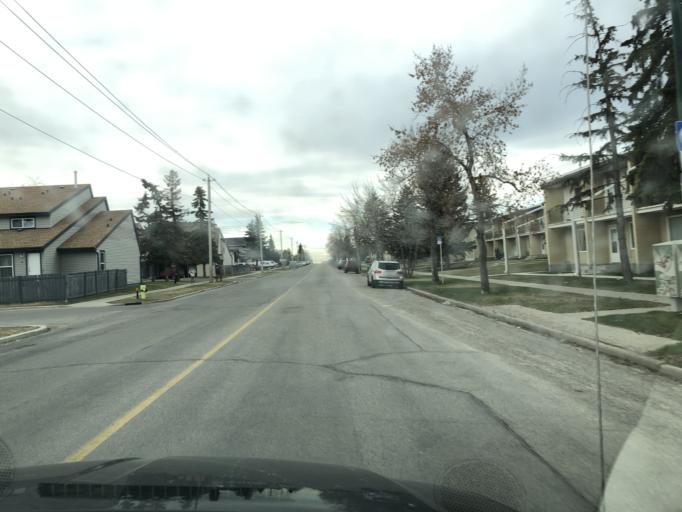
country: CA
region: Alberta
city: Calgary
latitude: 51.0742
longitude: -114.0134
